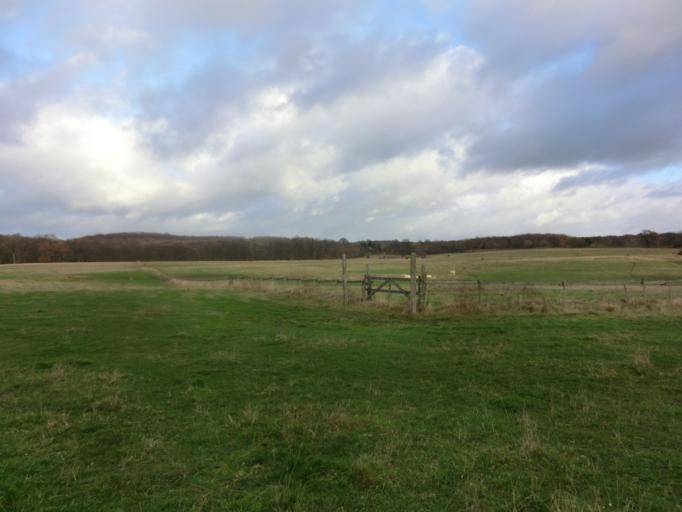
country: SE
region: Skane
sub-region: Lunds Kommun
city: Genarp
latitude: 55.6774
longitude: 13.3337
